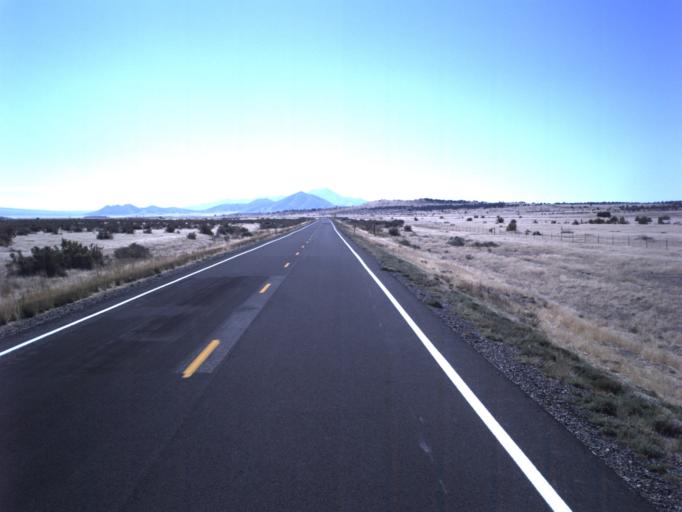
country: US
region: Utah
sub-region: Tooele County
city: Grantsville
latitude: 40.2671
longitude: -112.7412
